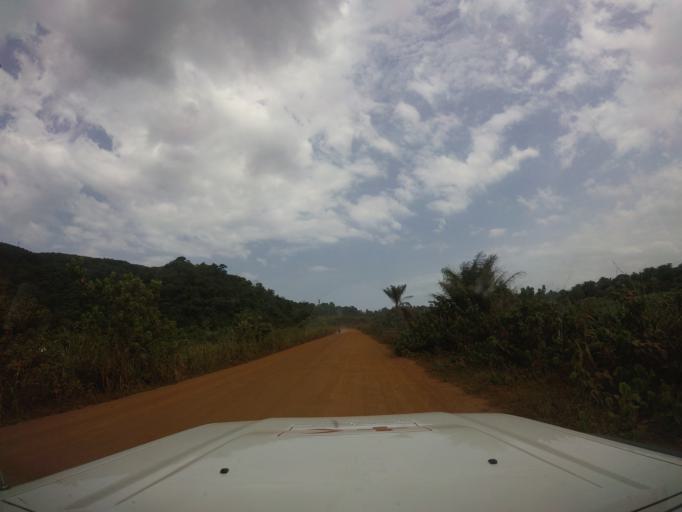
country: LR
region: Grand Cape Mount
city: Robertsport
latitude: 6.7494
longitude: -11.3595
